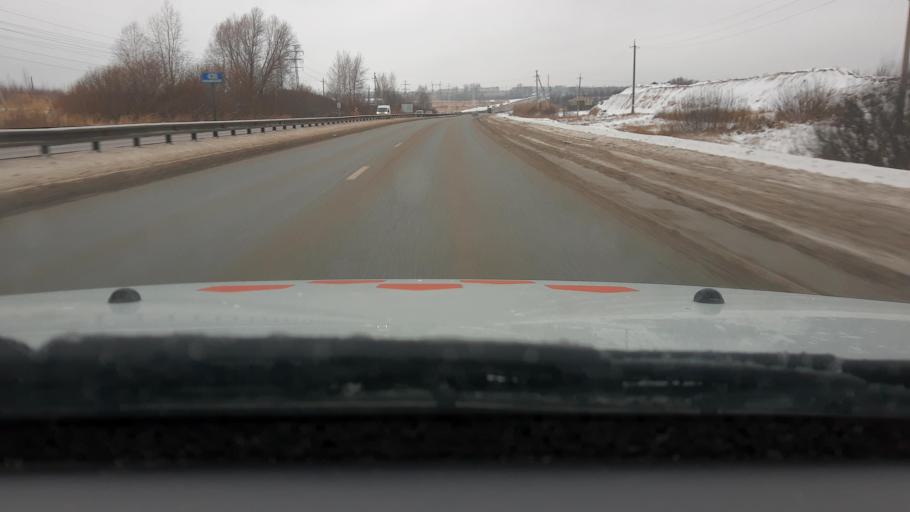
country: RU
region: Nizjnij Novgorod
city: Afonino
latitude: 56.1988
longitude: 44.1099
